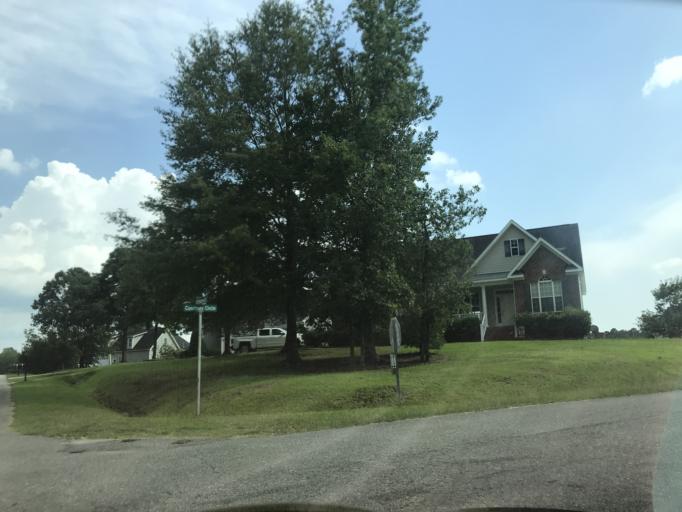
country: US
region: North Carolina
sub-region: Johnston County
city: Four Oaks
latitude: 35.5126
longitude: -78.5028
